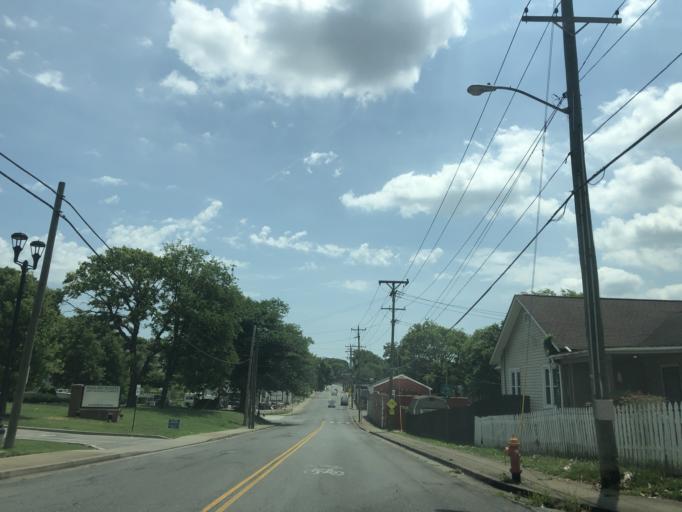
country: US
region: Tennessee
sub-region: Davidson County
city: Nashville
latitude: 36.1941
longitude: -86.7686
